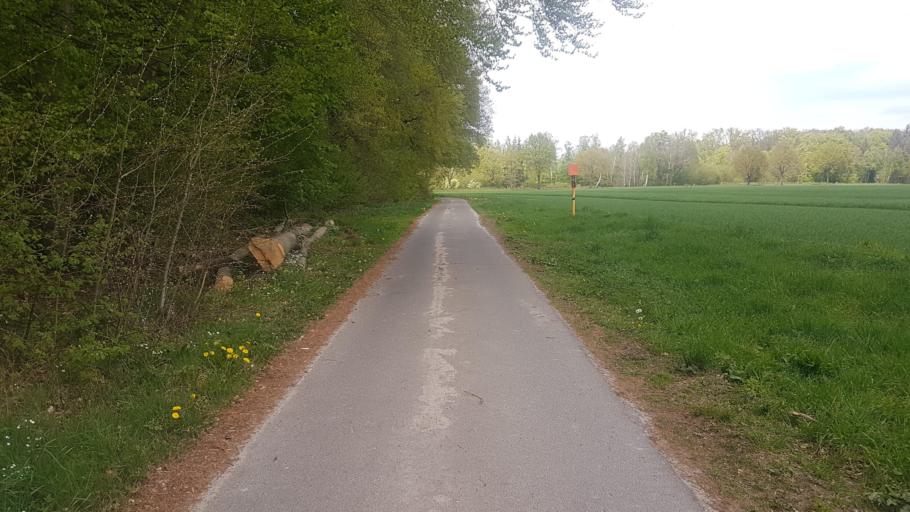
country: DE
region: Lower Saxony
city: Embsen
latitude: 53.2162
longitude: 10.3492
